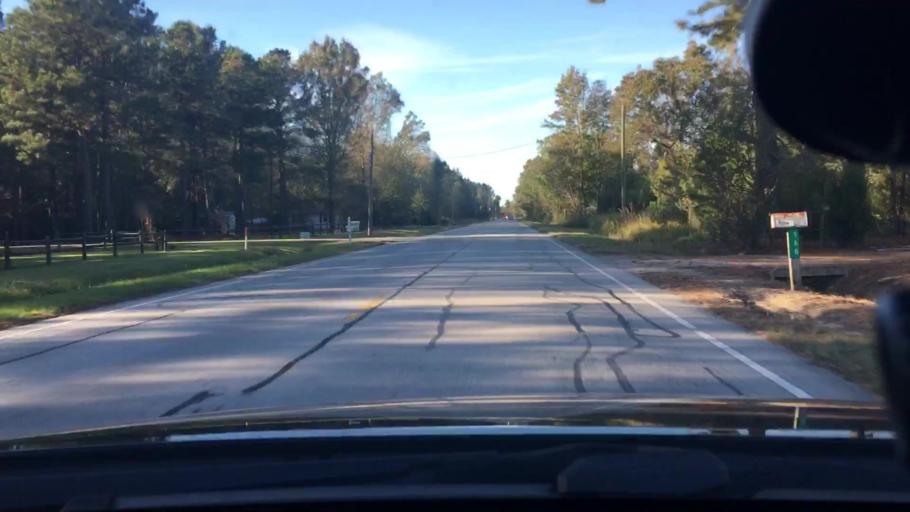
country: US
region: North Carolina
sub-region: Craven County
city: Vanceboro
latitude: 35.3220
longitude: -77.1659
